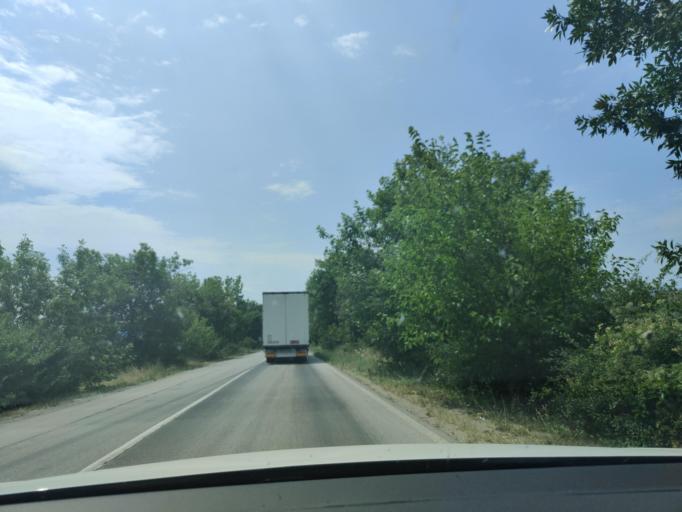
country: BG
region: Vidin
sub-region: Obshtina Ruzhintsi
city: Ruzhintsi
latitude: 43.6251
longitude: 22.8207
